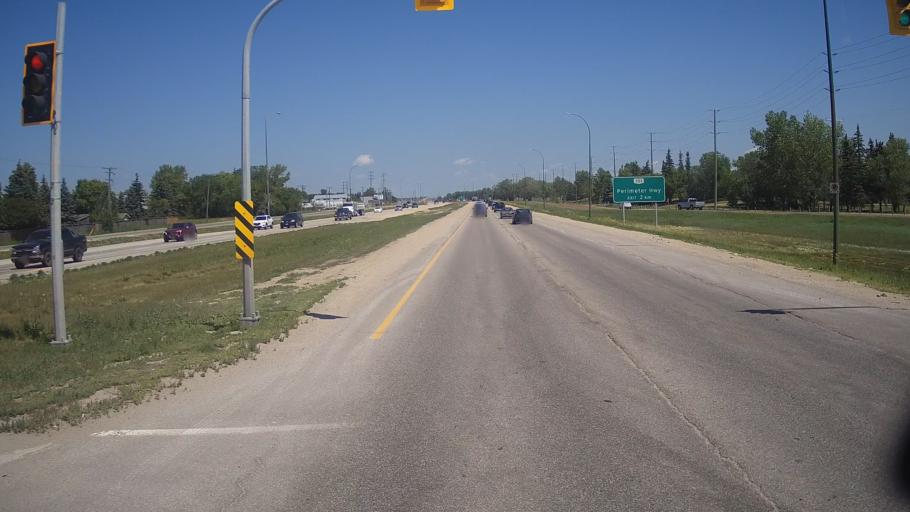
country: CA
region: Manitoba
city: Winnipeg
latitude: 49.9313
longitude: -97.0443
